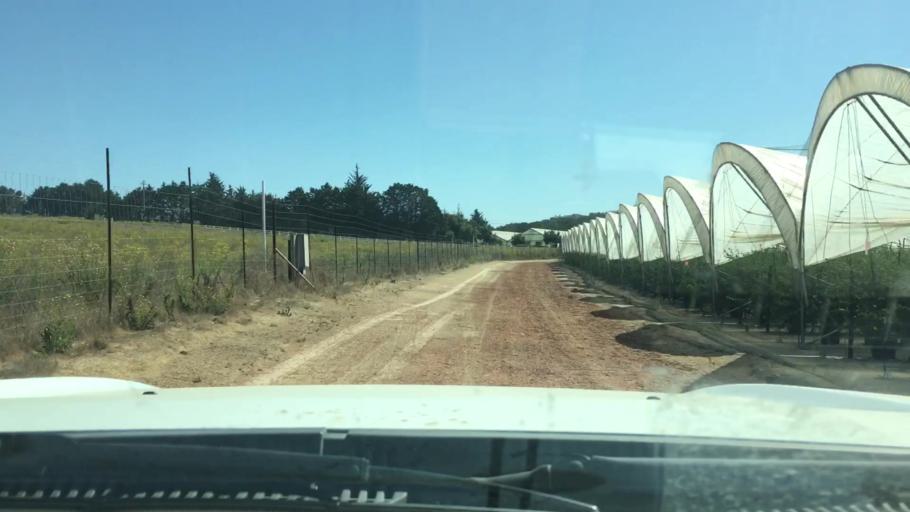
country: US
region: California
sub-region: San Luis Obispo County
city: Callender
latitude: 35.0646
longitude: -120.5636
